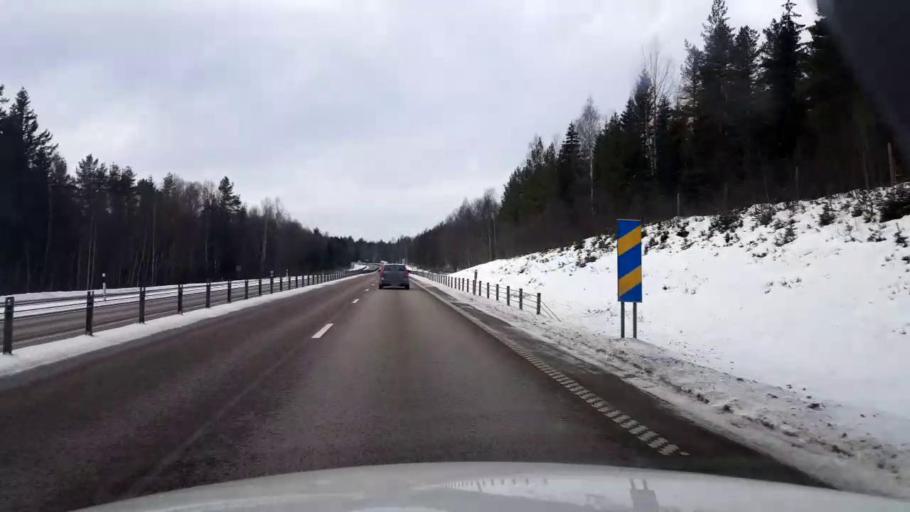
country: SE
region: Gaevleborg
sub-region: Hudiksvalls Kommun
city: Hudiksvall
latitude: 61.7911
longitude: 17.1502
